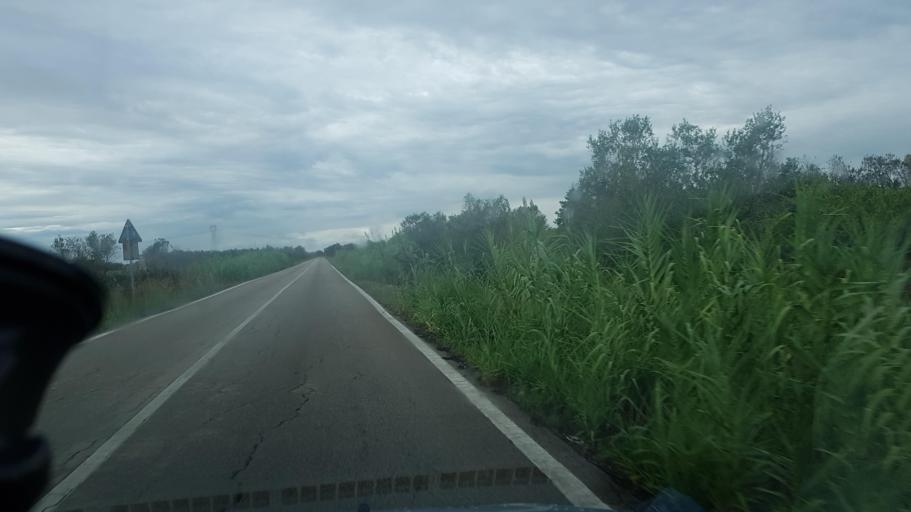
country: IT
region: Apulia
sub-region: Provincia di Lecce
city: Campi Salentina
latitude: 40.3647
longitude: 18.0037
